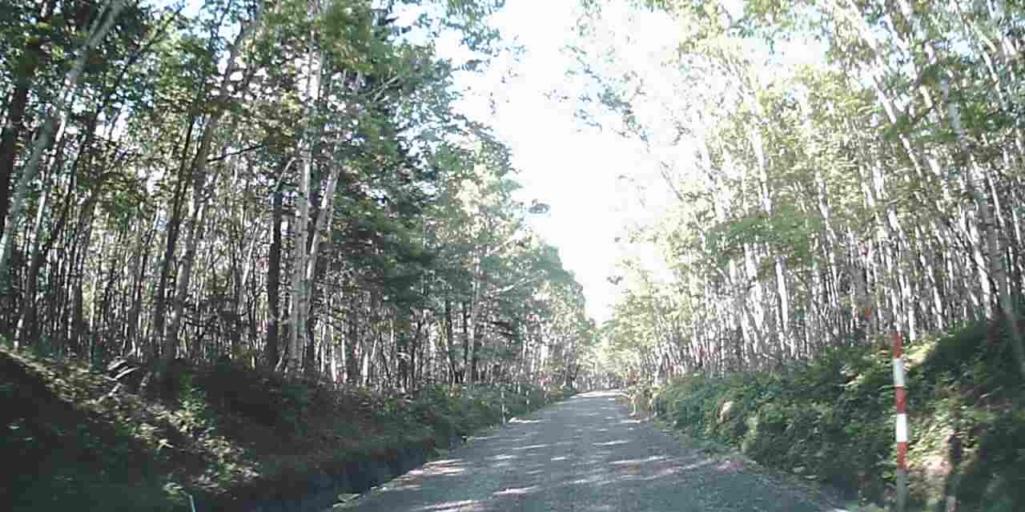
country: JP
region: Hokkaido
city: Shiraoi
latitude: 42.7070
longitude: 141.3968
